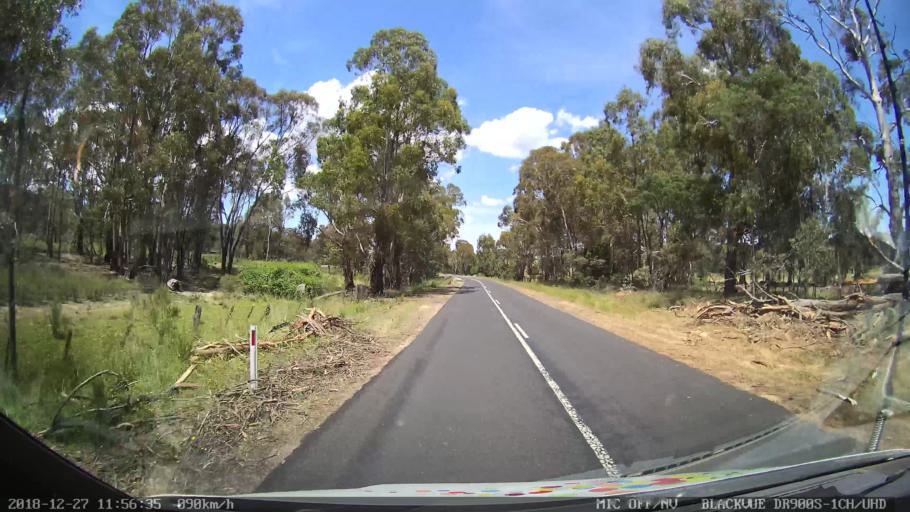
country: AU
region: New South Wales
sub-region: Blayney
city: Blayney
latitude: -33.7001
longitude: 149.3902
